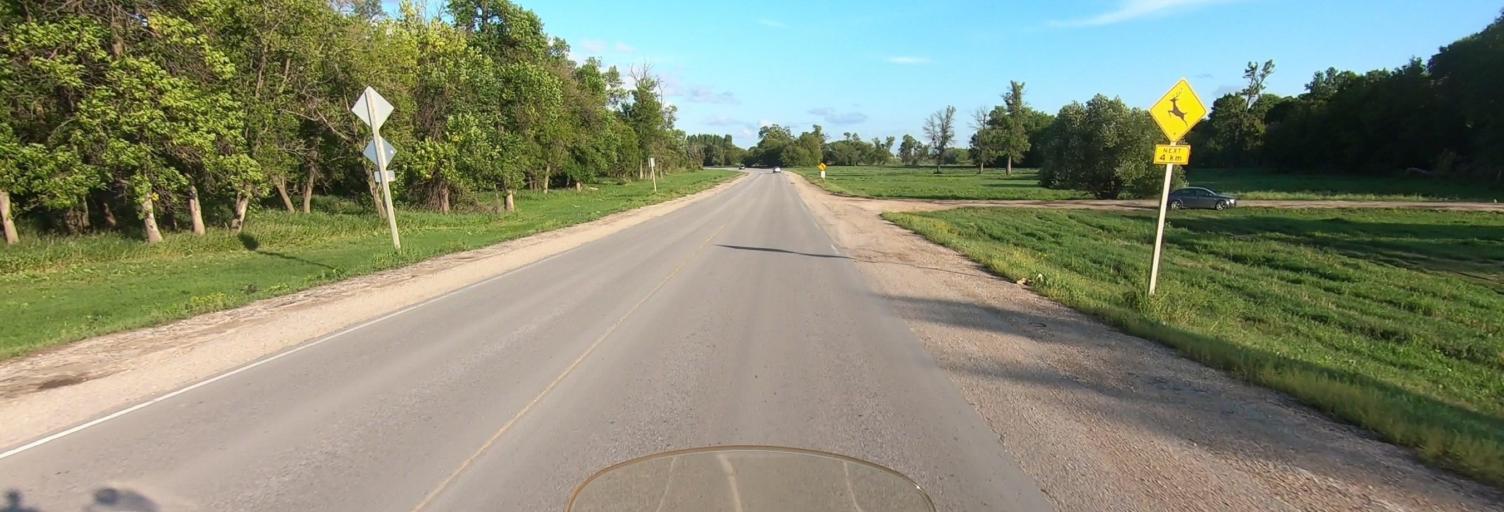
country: CA
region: Manitoba
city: Selkirk
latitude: 50.1396
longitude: -96.8665
